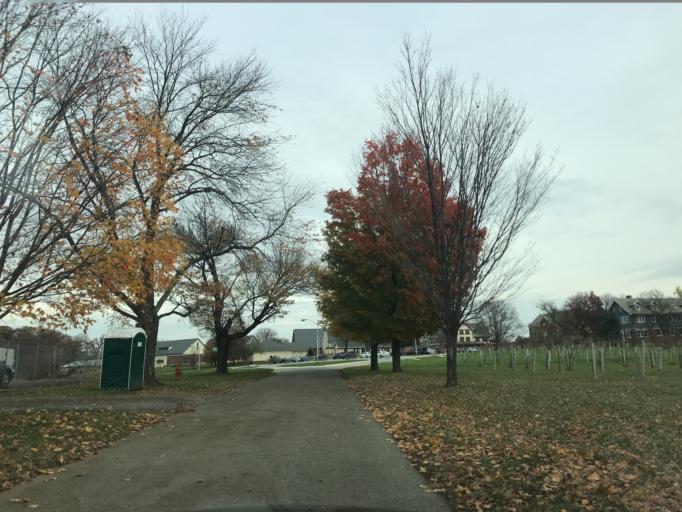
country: US
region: Maryland
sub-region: Baltimore County
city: Overlea
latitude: 39.3615
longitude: -76.5339
